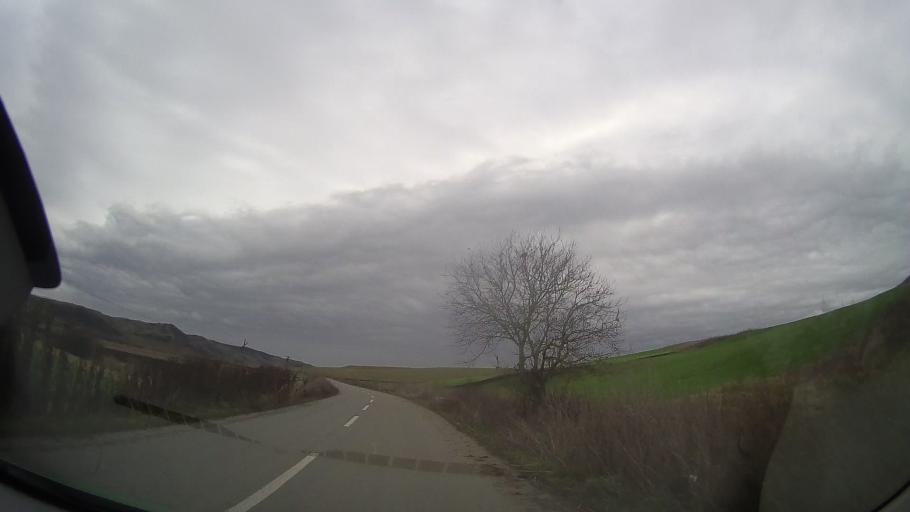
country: RO
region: Bistrita-Nasaud
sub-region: Comuna Milas
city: Milas
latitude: 46.7911
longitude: 24.4215
